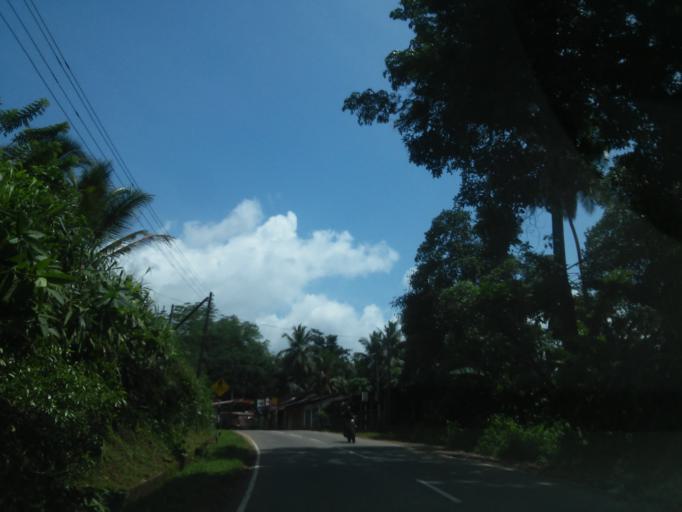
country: LK
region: Sabaragamuwa
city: Ratnapura
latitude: 6.7302
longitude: 80.3179
